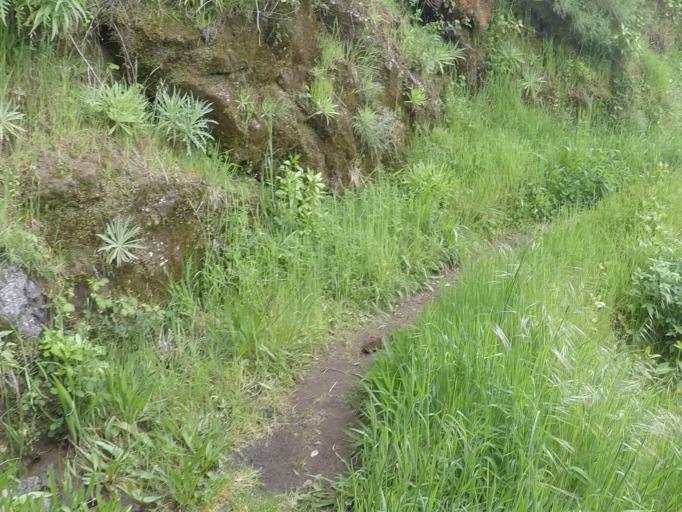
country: PT
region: Madeira
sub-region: Camara de Lobos
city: Curral das Freiras
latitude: 32.7344
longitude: -17.0002
